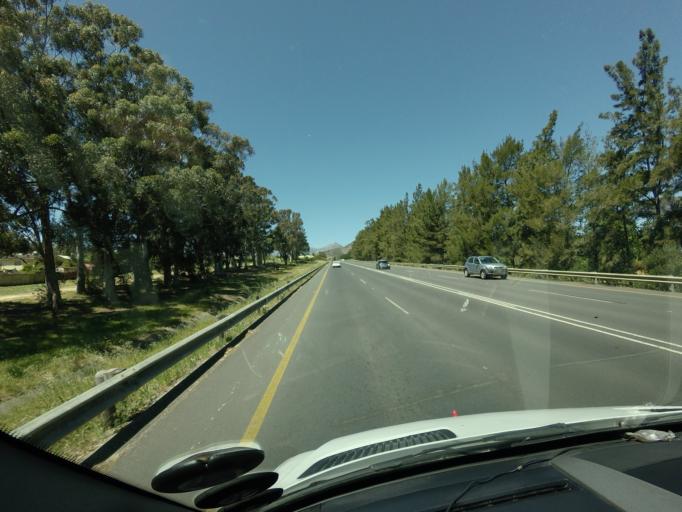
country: ZA
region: Western Cape
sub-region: Cape Winelands District Municipality
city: Stellenbosch
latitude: -33.9258
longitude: 18.8850
